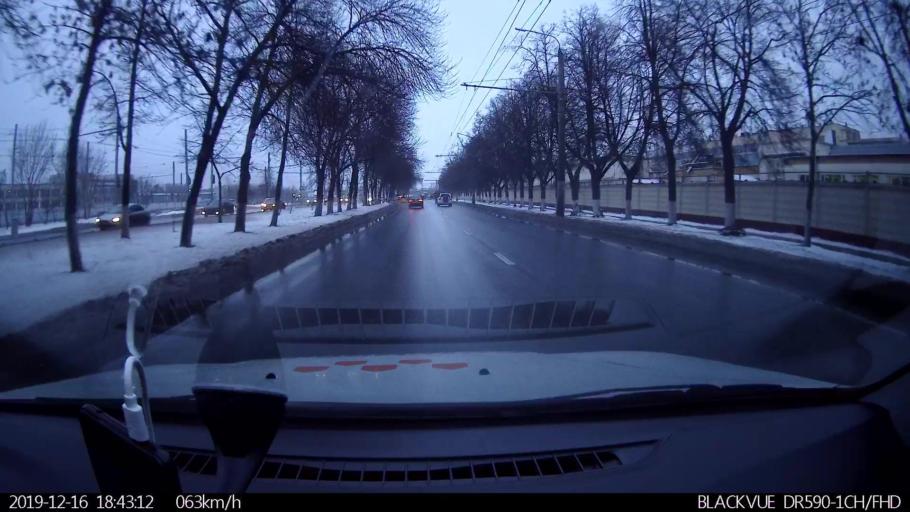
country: RU
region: Nizjnij Novgorod
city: Nizhniy Novgorod
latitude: 56.2555
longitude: 43.8990
